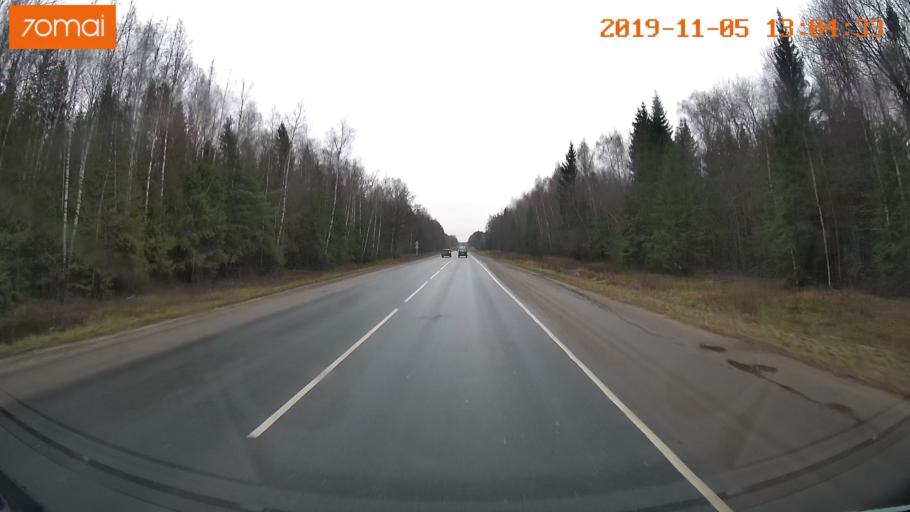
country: RU
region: Ivanovo
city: Kitovo
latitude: 56.8883
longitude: 41.2237
